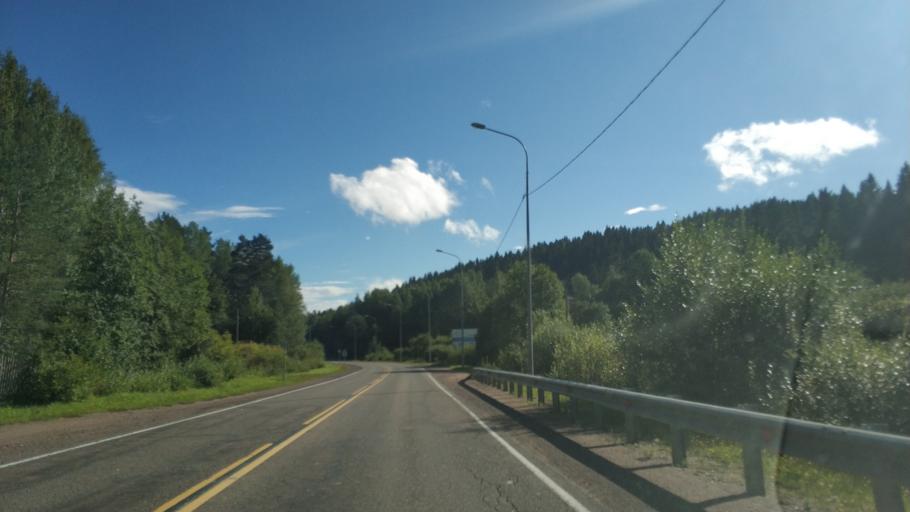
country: RU
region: Republic of Karelia
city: Sortavala
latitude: 61.6678
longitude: 30.6539
